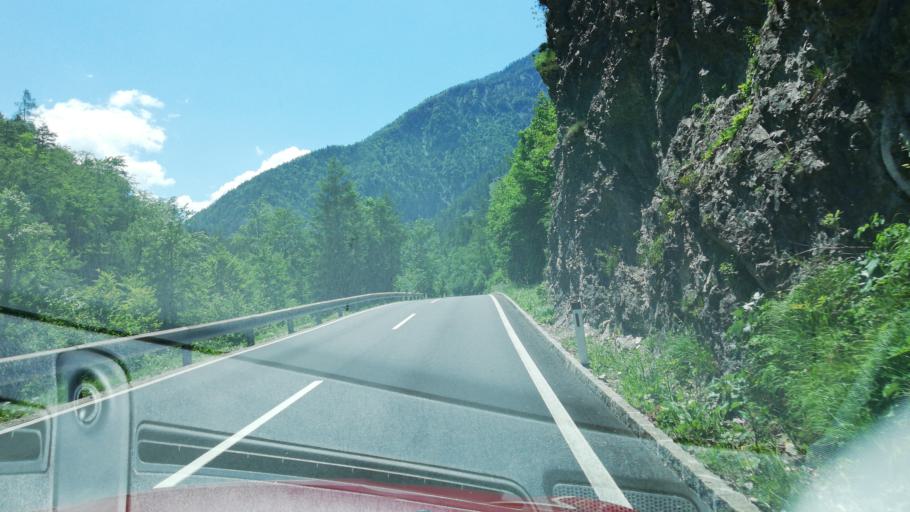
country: AT
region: Upper Austria
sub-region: Politischer Bezirk Kirchdorf an der Krems
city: Rossleithen
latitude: 47.7557
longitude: 14.1638
